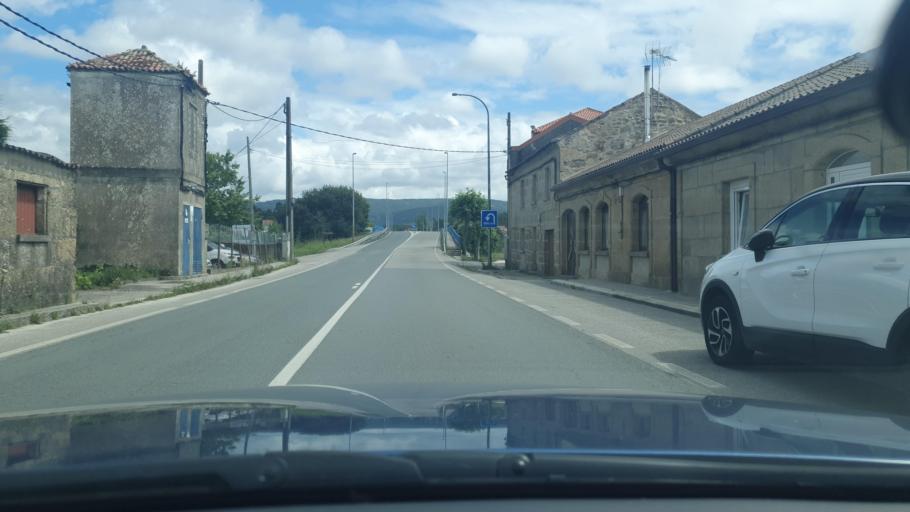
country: ES
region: Galicia
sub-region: Provincia de Pontevedra
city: Cambados
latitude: 42.5029
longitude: -8.8075
